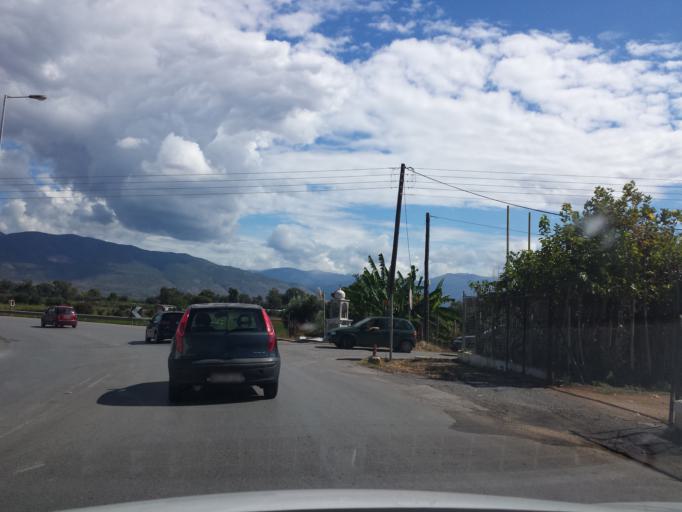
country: GR
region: Peloponnese
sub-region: Nomos Messinias
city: Messini
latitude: 37.0472
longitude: 22.0124
